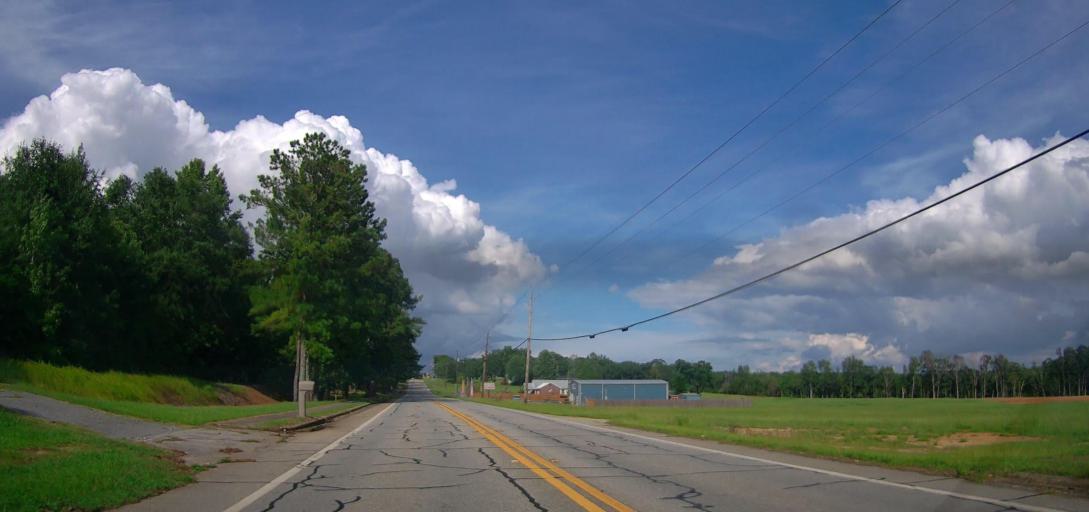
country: US
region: Georgia
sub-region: Harris County
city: Hamilton
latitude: 32.6508
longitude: -84.8727
